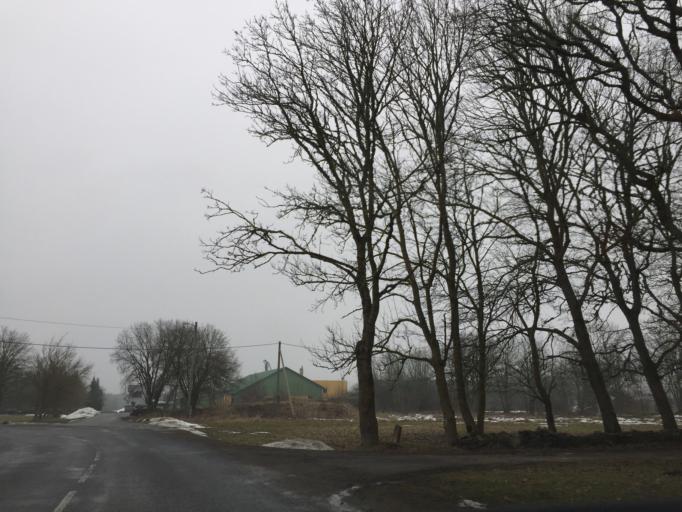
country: EE
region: Saare
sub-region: Kuressaare linn
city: Kuressaare
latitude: 58.3036
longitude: 22.8190
